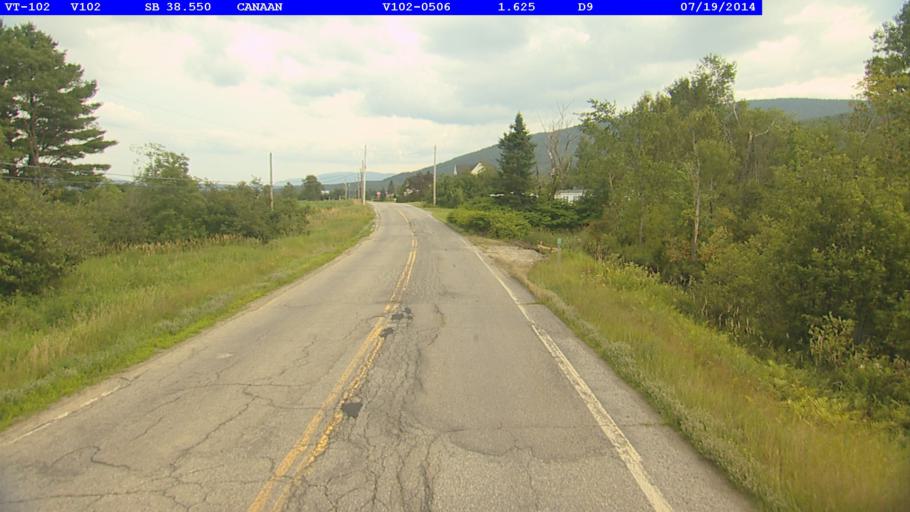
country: US
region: New Hampshire
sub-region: Coos County
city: Colebrook
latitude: 44.9303
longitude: -71.5239
